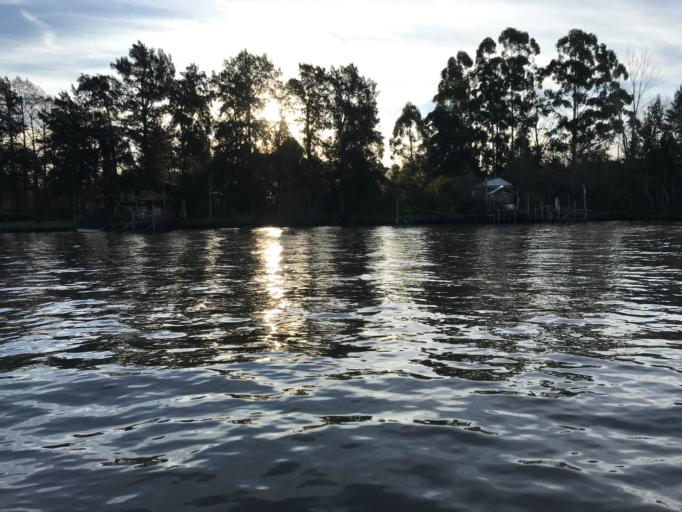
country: AR
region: Buenos Aires
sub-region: Partido de Tigre
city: Tigre
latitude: -34.3816
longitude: -58.5749
